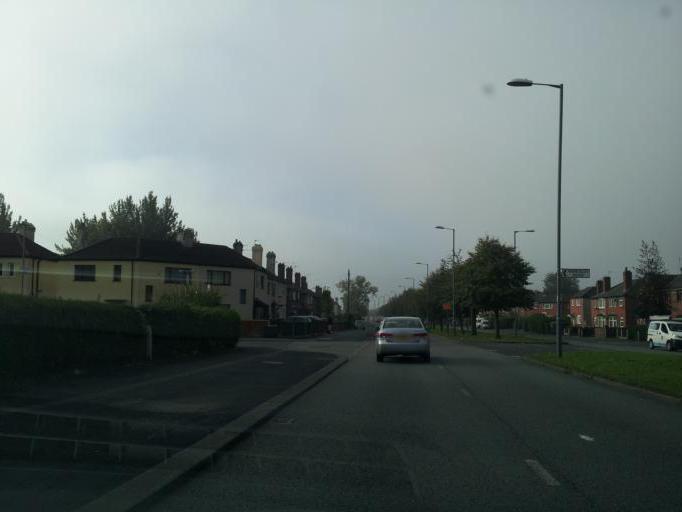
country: GB
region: England
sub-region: Manchester
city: Failsworth
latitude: 53.5193
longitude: -2.1674
